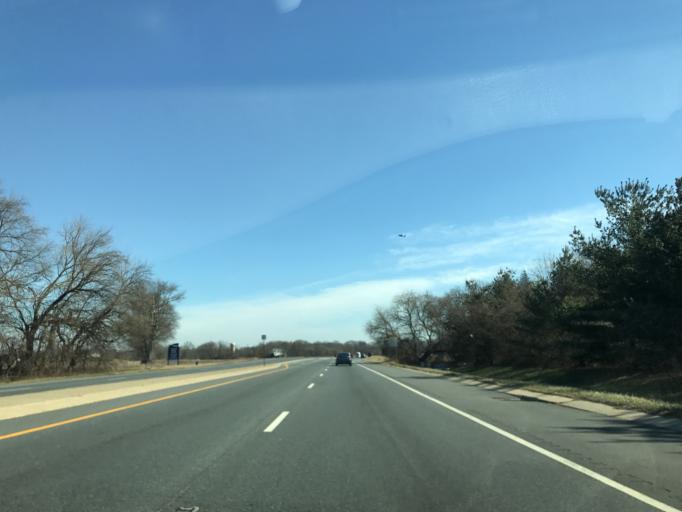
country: US
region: Delaware
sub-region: New Castle County
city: Glasgow
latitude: 39.5296
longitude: -75.7299
